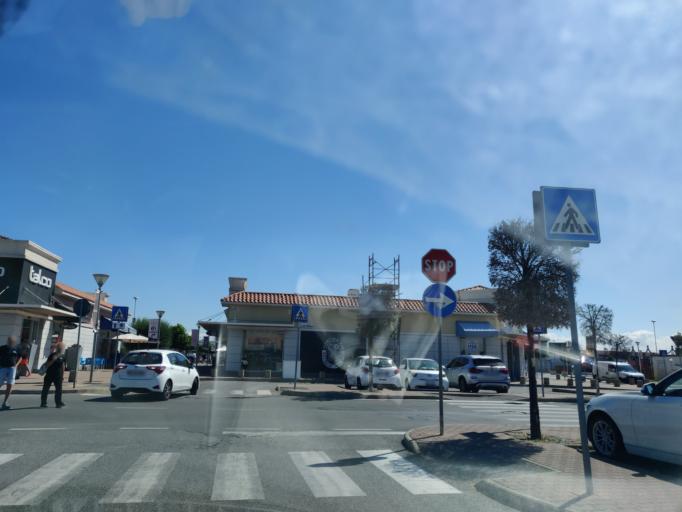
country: IT
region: Latium
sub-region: Citta metropolitana di Roma Capitale
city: Npp 23 (Parco Leonardo)
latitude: 41.8087
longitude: 12.2998
